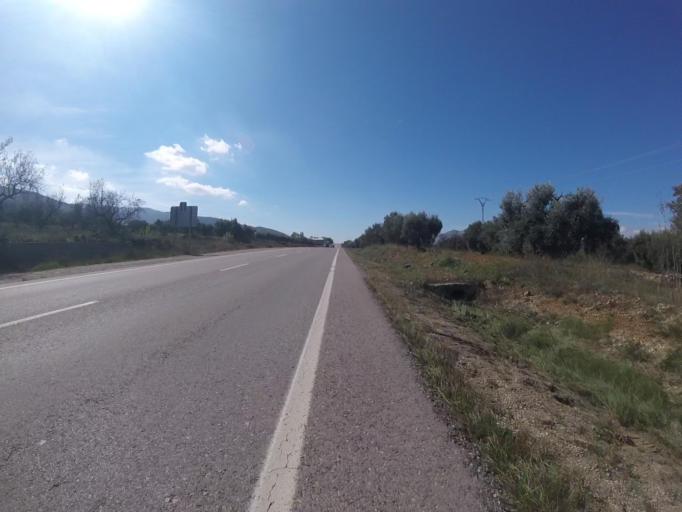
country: ES
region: Valencia
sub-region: Provincia de Castello
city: Albocasser
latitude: 40.3393
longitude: -0.0093
